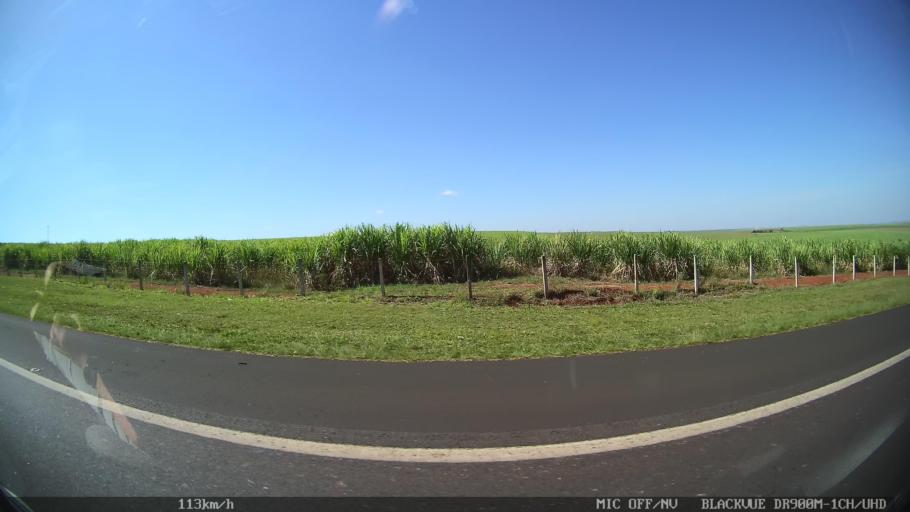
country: BR
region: Sao Paulo
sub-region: Franca
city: Franca
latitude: -20.6829
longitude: -47.4962
